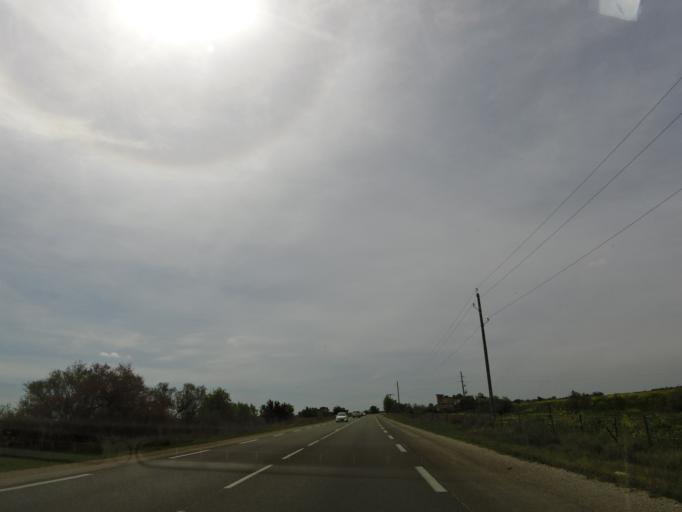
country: FR
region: Languedoc-Roussillon
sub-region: Departement de l'Herault
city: Saint-Just
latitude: 43.6293
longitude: 4.1295
